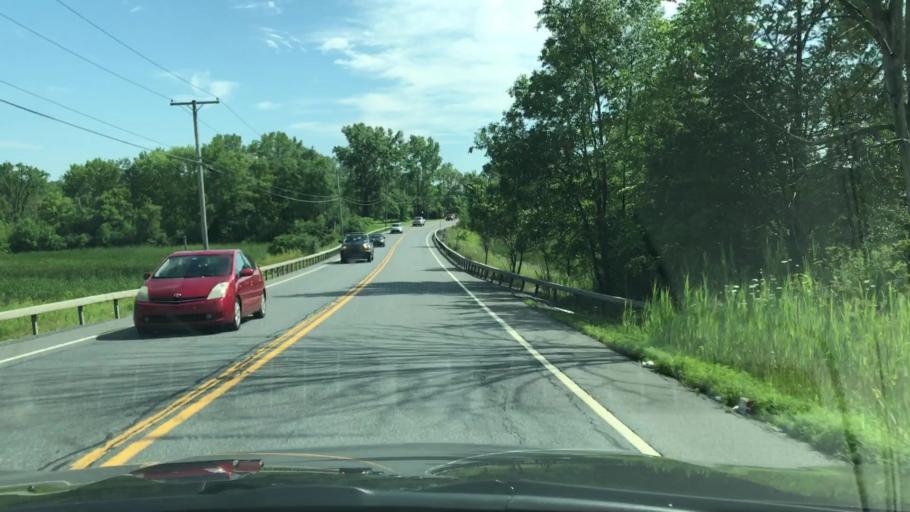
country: US
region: New York
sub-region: Washington County
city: Whitehall
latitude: 43.5205
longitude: -73.4141
